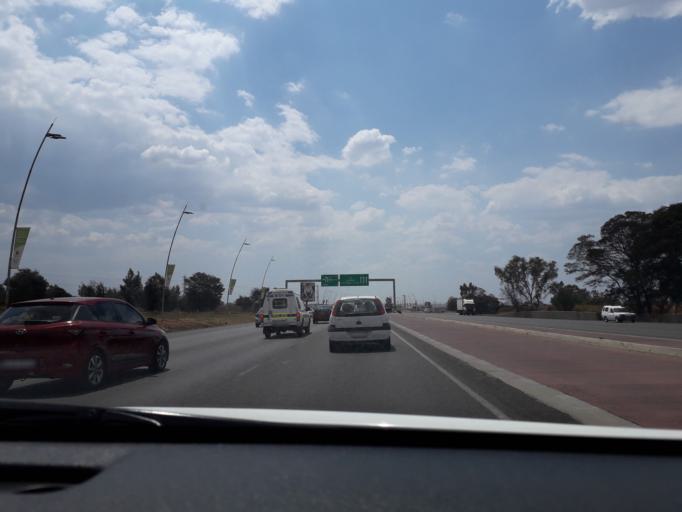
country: ZA
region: Gauteng
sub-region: City of Johannesburg Metropolitan Municipality
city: Modderfontein
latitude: -26.0640
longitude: 28.1852
